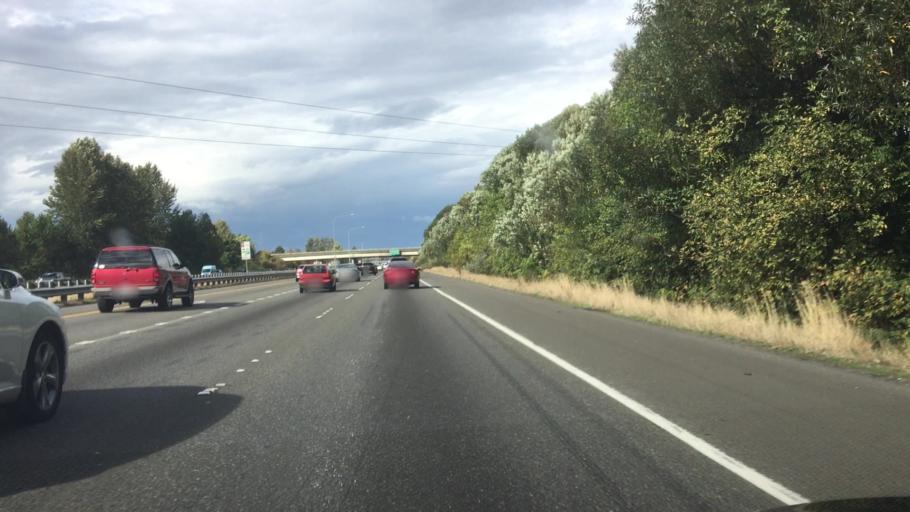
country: US
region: Washington
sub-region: King County
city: Lakeland North
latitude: 47.3365
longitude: -122.2447
